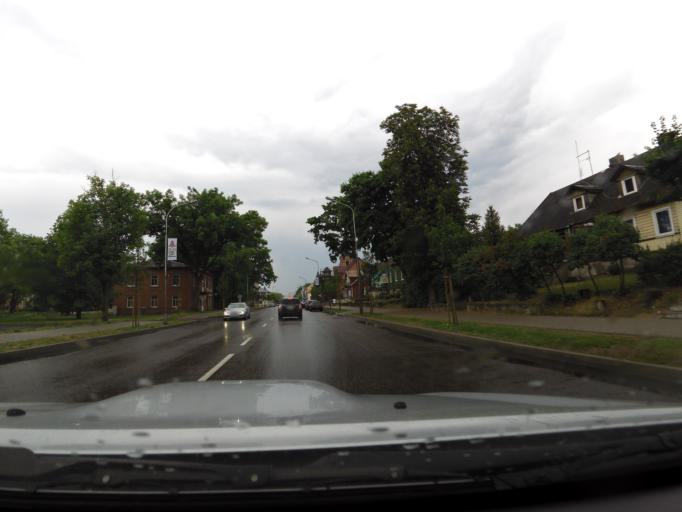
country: LT
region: Marijampoles apskritis
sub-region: Marijampole Municipality
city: Marijampole
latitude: 54.5503
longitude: 23.3480
